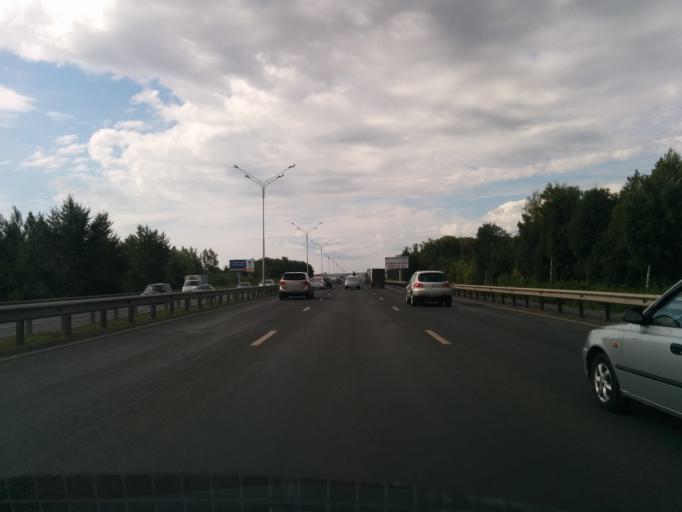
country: RU
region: Bashkortostan
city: Ufa
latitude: 54.6874
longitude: 55.9386
